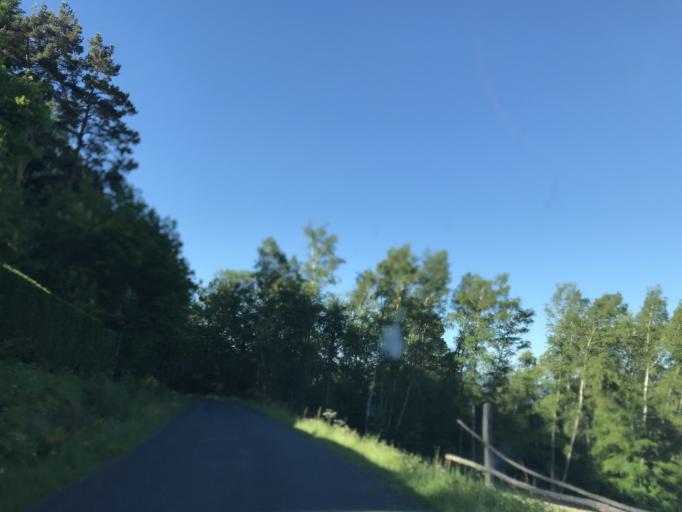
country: FR
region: Auvergne
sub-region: Departement du Puy-de-Dome
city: Job
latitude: 45.6979
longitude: 3.6848
